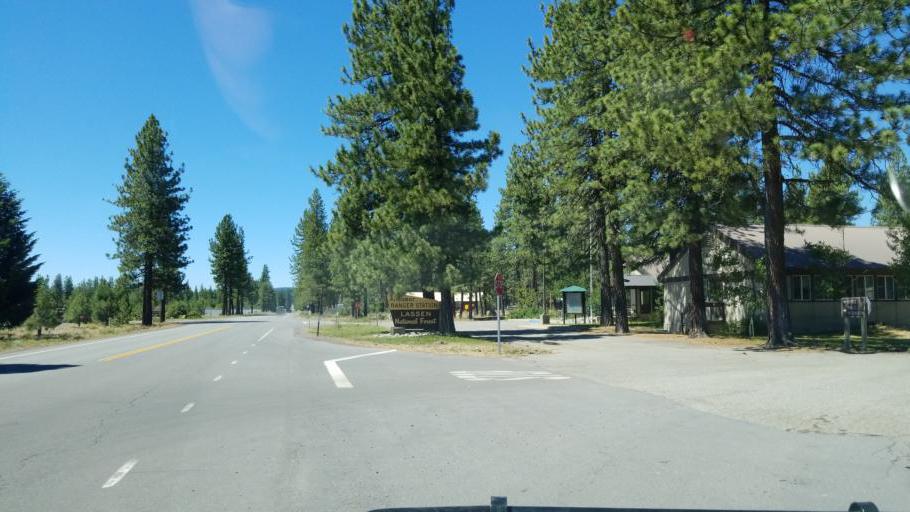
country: US
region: California
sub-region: Plumas County
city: Chester
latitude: 40.2904
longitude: -121.2445
